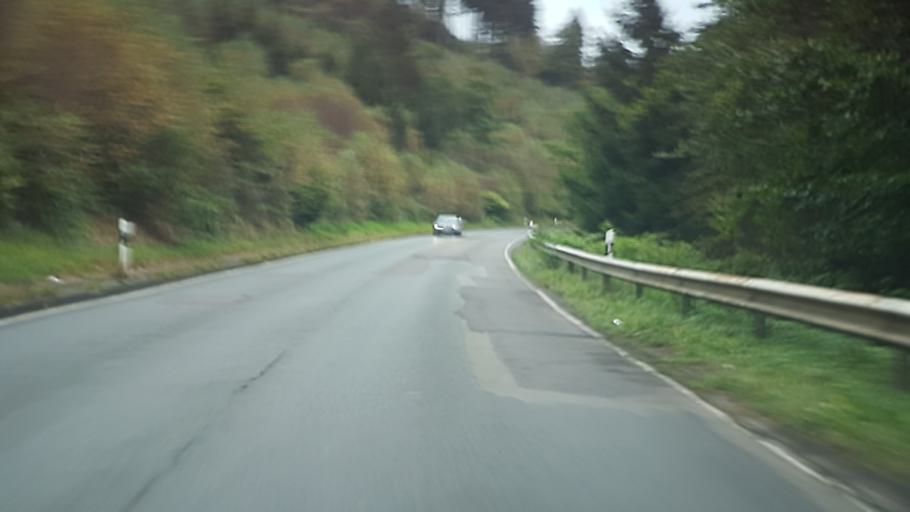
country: DE
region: North Rhine-Westphalia
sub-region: Regierungsbezirk Arnsberg
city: Attendorn
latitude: 51.1490
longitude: 7.8494
